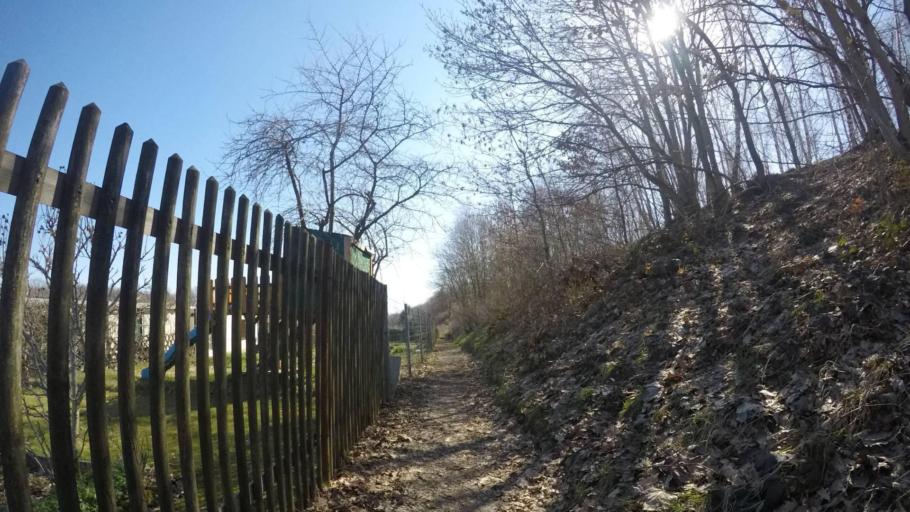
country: DE
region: Saxony
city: Limbach-Oberfrohna
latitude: 50.8608
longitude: 12.7776
